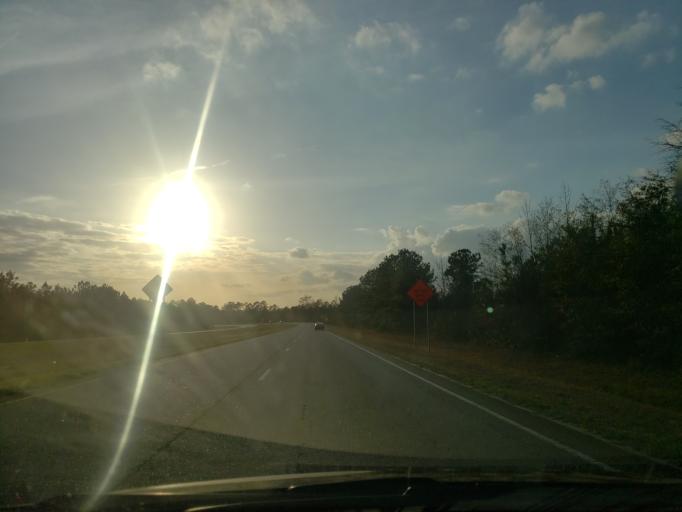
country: US
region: Georgia
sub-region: Chatham County
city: Bloomingdale
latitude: 32.1468
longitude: -81.3011
